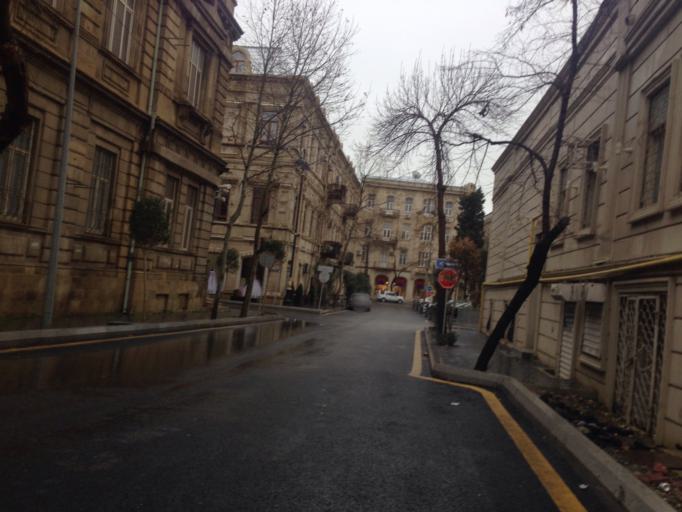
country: AZ
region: Baki
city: Baku
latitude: 40.3763
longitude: 49.8443
